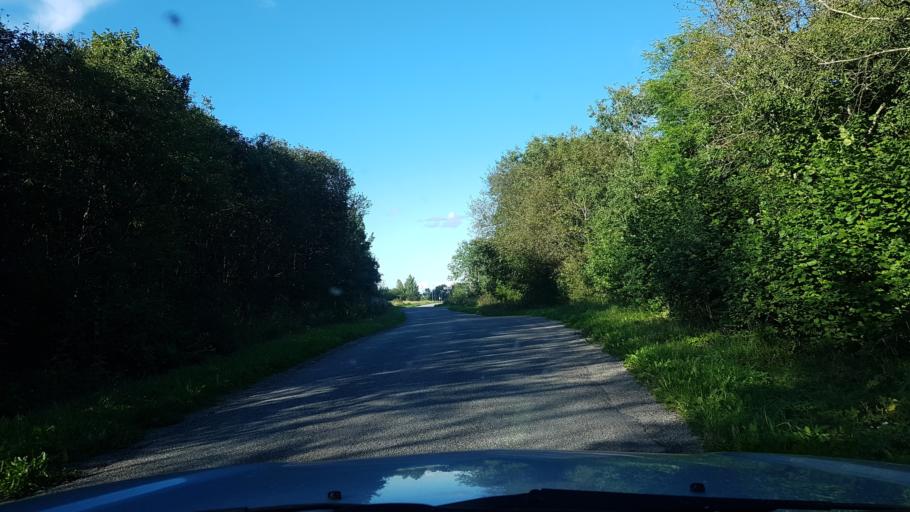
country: EE
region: Harju
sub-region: Kiili vald
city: Kiili
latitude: 59.3304
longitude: 24.8324
